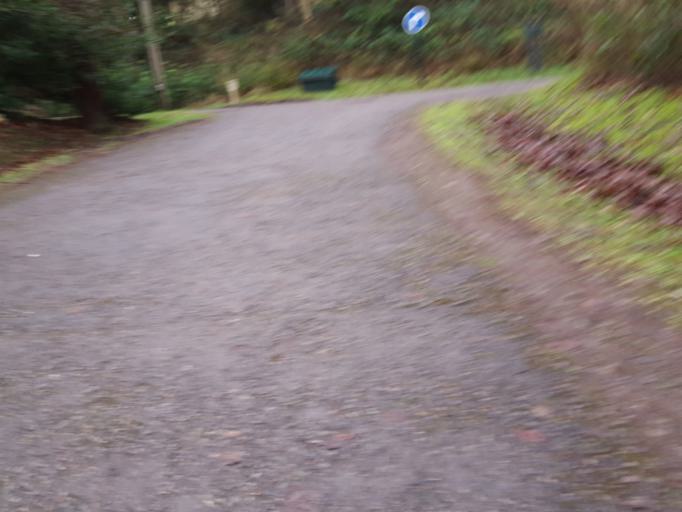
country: GB
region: England
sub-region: Wiltshire
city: Corsley
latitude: 51.1896
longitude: -2.2316
